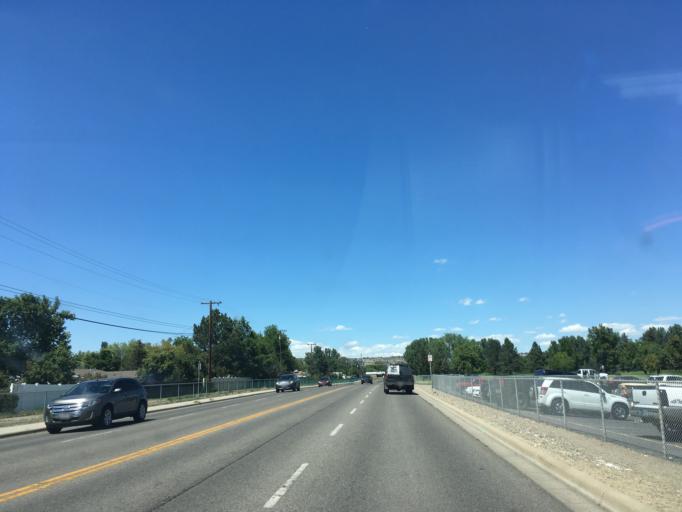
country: US
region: Montana
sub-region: Yellowstone County
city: Billings
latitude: 45.7655
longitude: -108.5650
